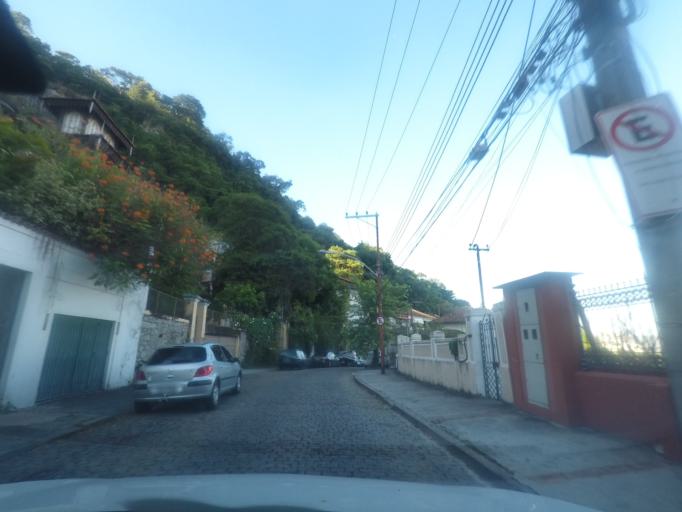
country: BR
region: Rio de Janeiro
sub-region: Rio De Janeiro
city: Rio de Janeiro
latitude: -22.9250
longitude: -43.1874
